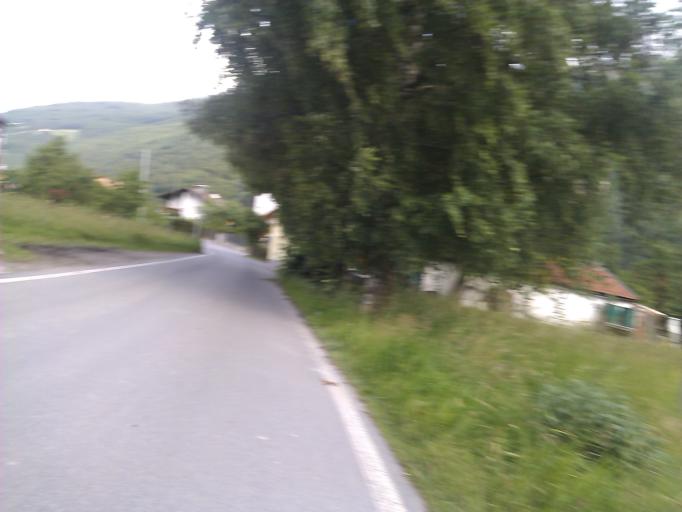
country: IT
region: Trentino-Alto Adige
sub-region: Bolzano
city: Lasa
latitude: 46.6159
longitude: 10.6945
